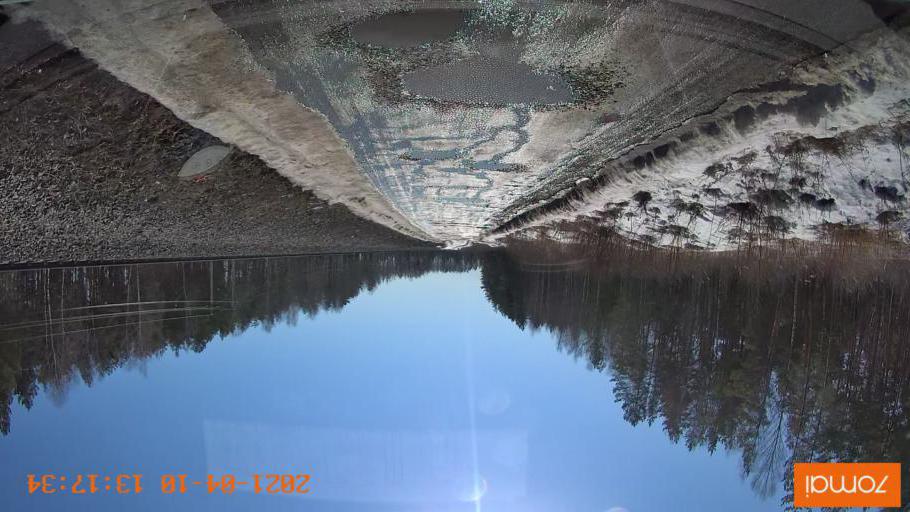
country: RU
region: Ivanovo
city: Kokhma
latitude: 56.9947
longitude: 41.0589
